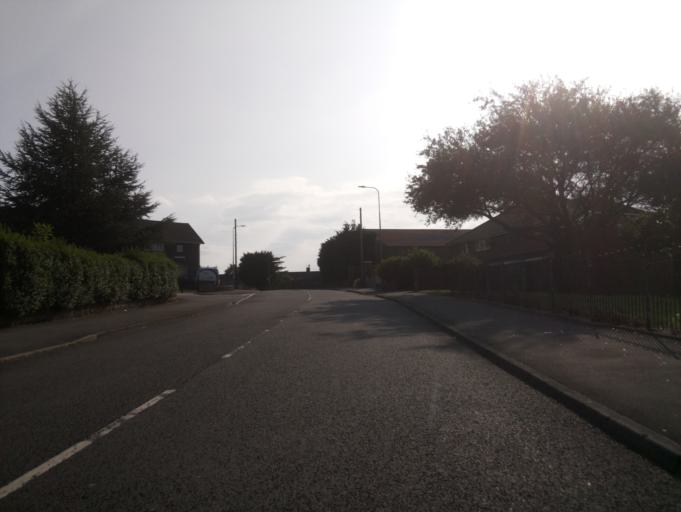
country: GB
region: Wales
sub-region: Newport
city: Marshfield
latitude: 51.5229
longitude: -3.1234
